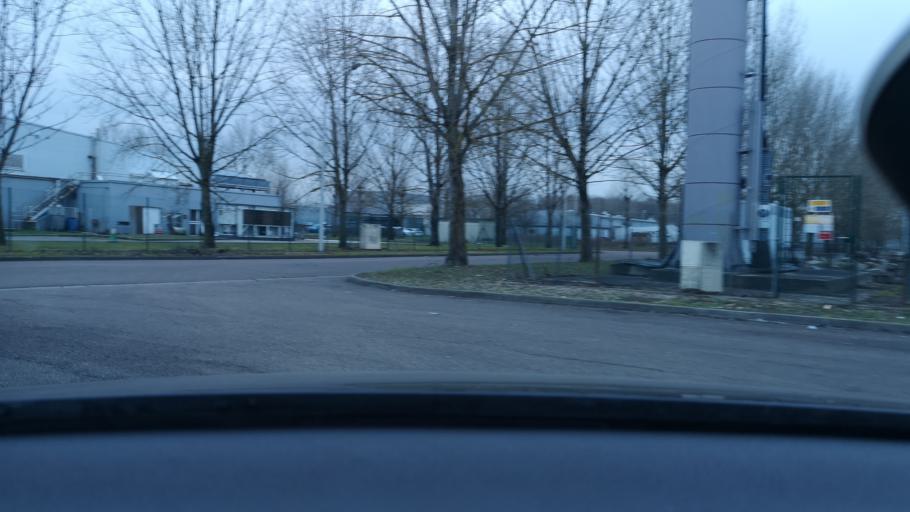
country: FR
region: Bourgogne
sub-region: Departement de Saone-et-Loire
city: Chalon-sur-Saone
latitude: 46.7704
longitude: 4.8621
